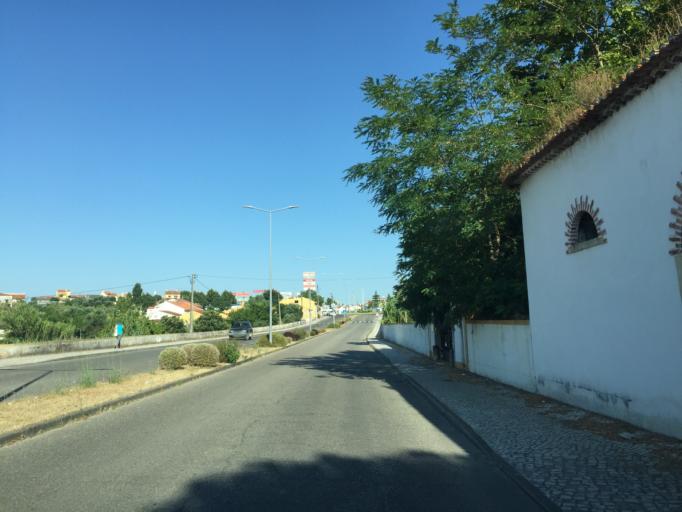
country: PT
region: Santarem
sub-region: Tomar
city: Tomar
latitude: 39.6015
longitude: -8.3930
